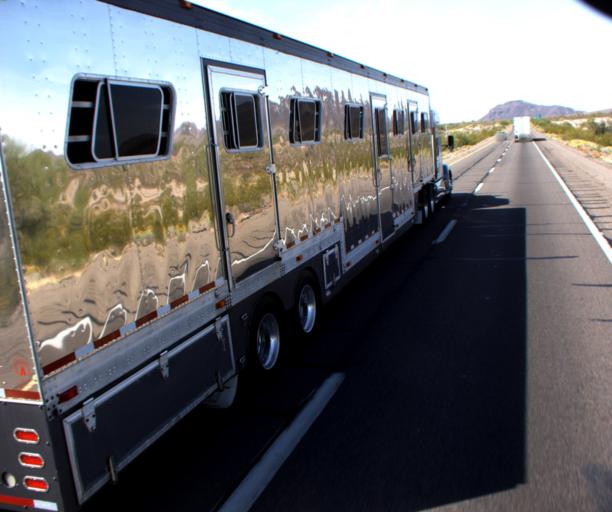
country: US
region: Arizona
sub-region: La Paz County
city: Quartzsite
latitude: 33.6594
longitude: -113.9889
